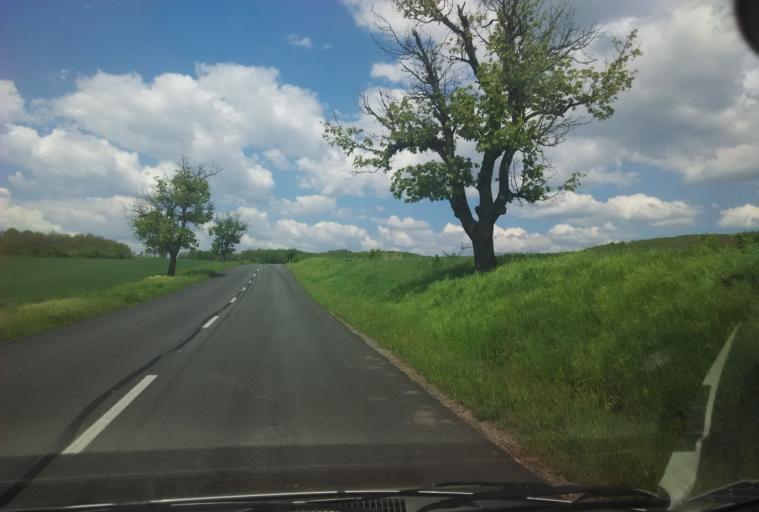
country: SK
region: Banskobystricky
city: Dudince
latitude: 48.2106
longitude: 18.7874
